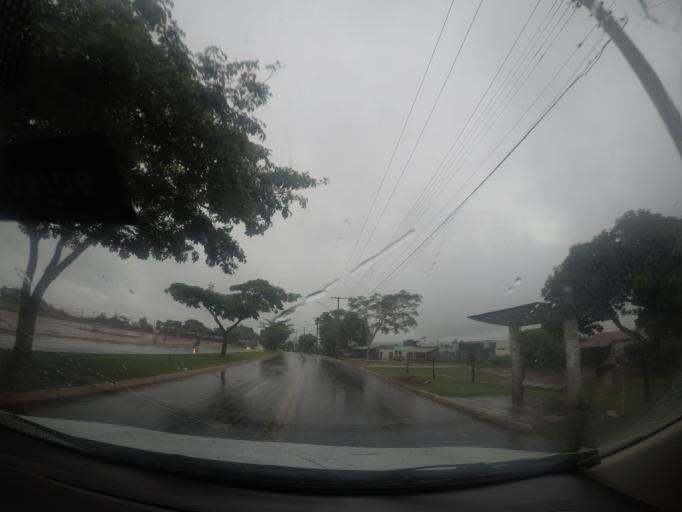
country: BR
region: Goias
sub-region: Goiania
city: Goiania
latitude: -16.6026
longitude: -49.3331
